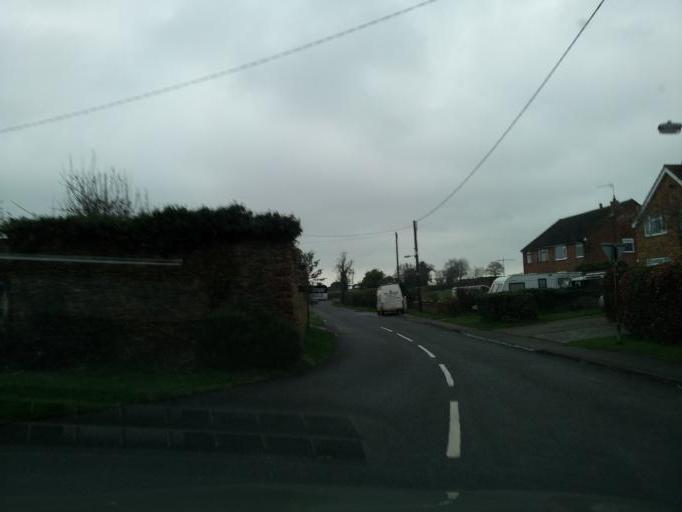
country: GB
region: England
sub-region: Warwickshire
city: Rugby
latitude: 52.3308
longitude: -1.2005
